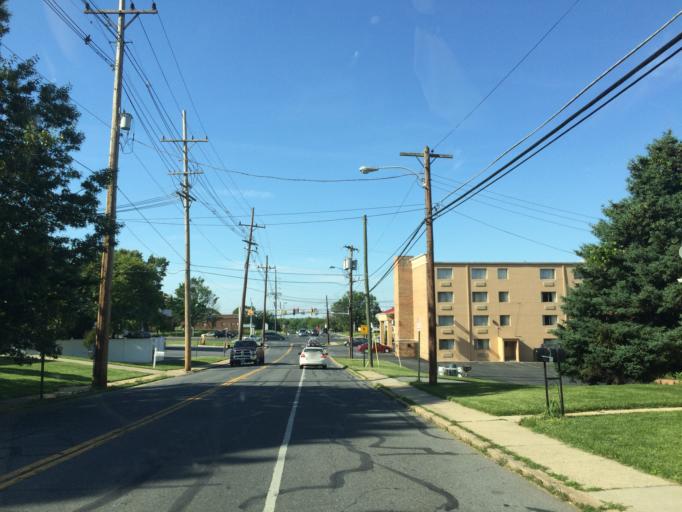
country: US
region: Maryland
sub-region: Frederick County
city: Frederick
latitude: 39.4150
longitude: -77.4390
